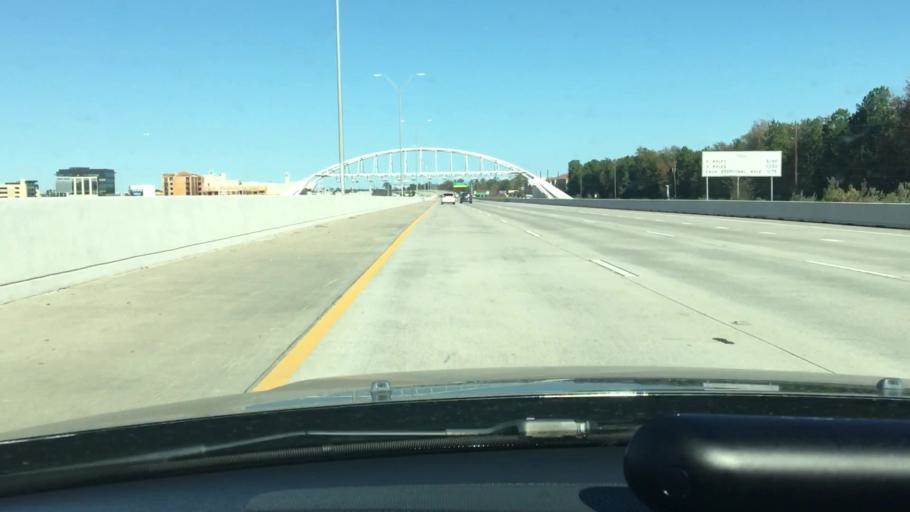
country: US
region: Texas
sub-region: Harris County
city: Sheldon
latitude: 29.9138
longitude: -95.2012
